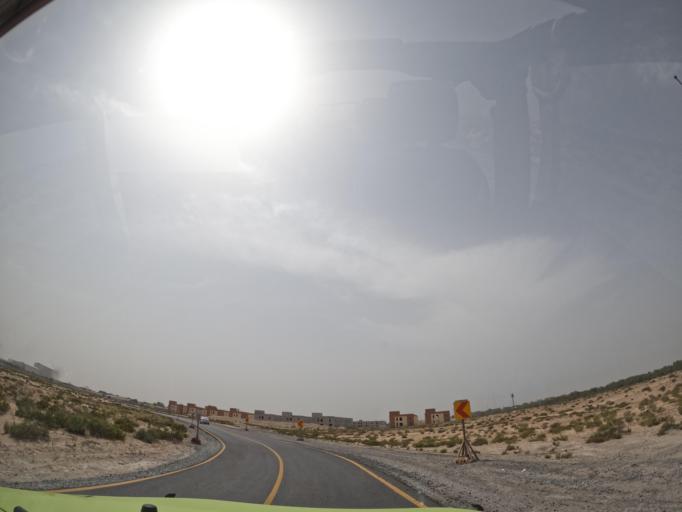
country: AE
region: Dubai
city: Dubai
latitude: 25.1313
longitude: 55.3401
